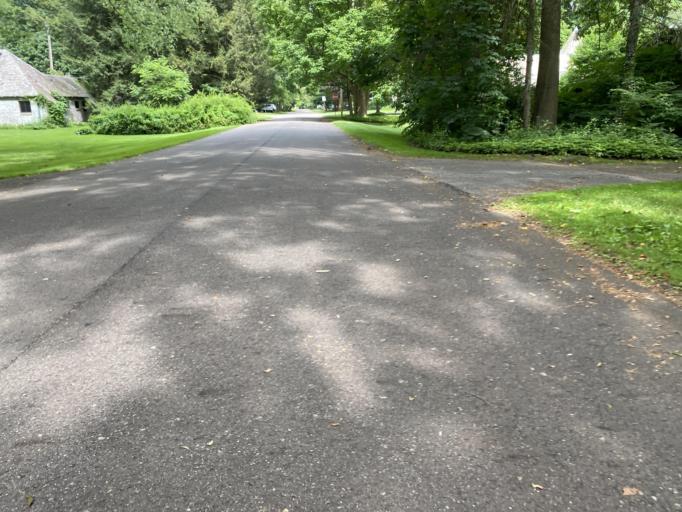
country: US
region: Ohio
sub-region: Summit County
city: Fairlawn
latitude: 41.1134
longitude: -81.5859
